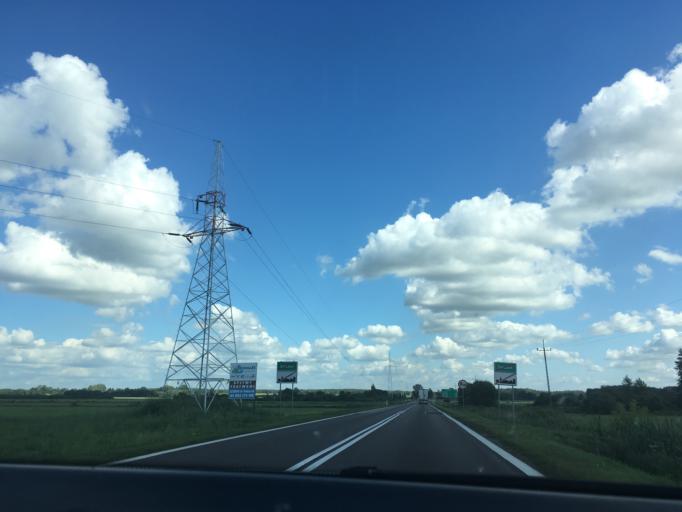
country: PL
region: Podlasie
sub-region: Powiat sokolski
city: Suchowola
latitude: 53.6766
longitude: 23.1060
